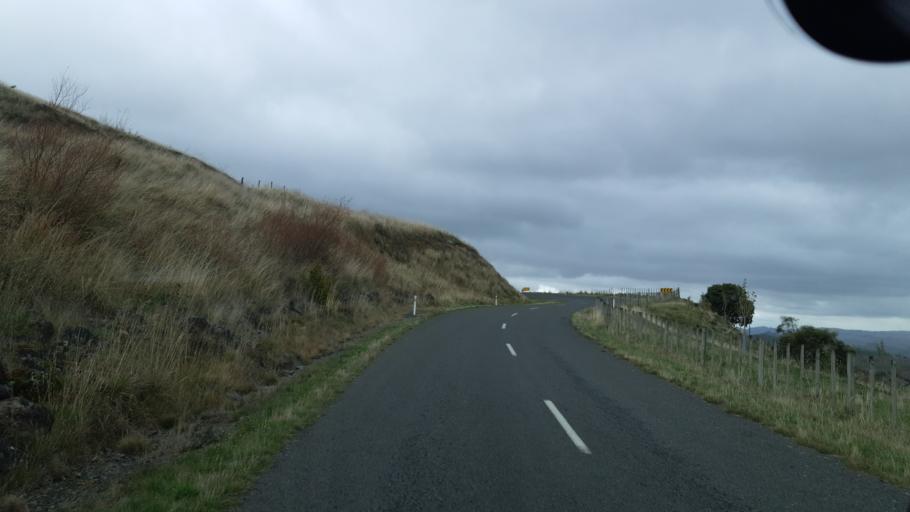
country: NZ
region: Manawatu-Wanganui
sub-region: Ruapehu District
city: Waiouru
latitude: -39.6155
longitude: 175.6498
